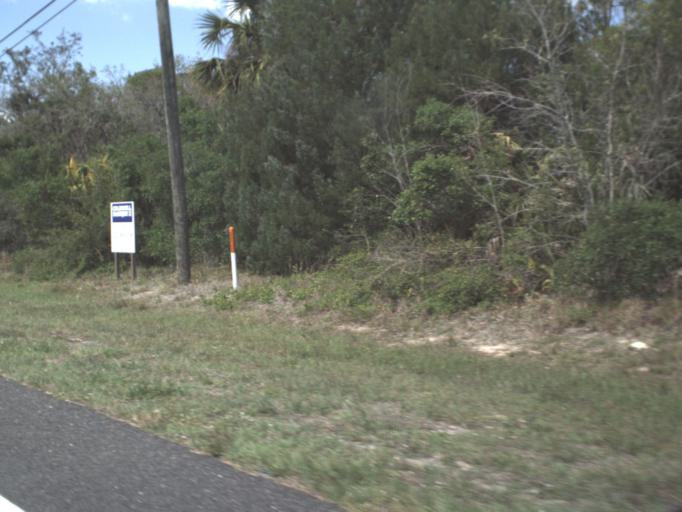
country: US
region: Florida
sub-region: Brevard County
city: Mims
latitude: 28.7151
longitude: -80.8632
